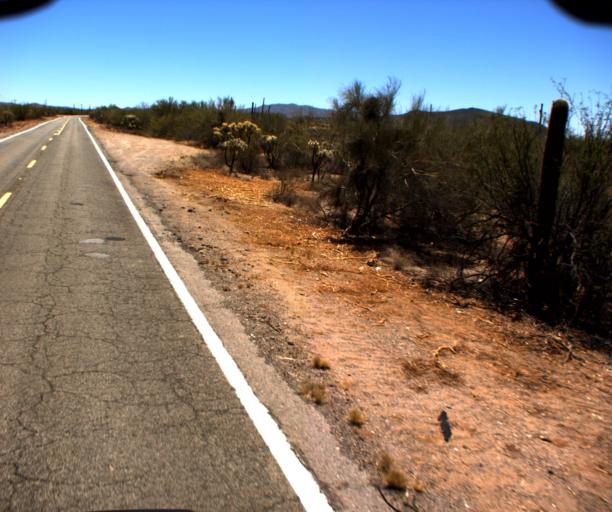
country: US
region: Arizona
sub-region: Pima County
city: Sells
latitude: 32.1821
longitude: -112.2853
